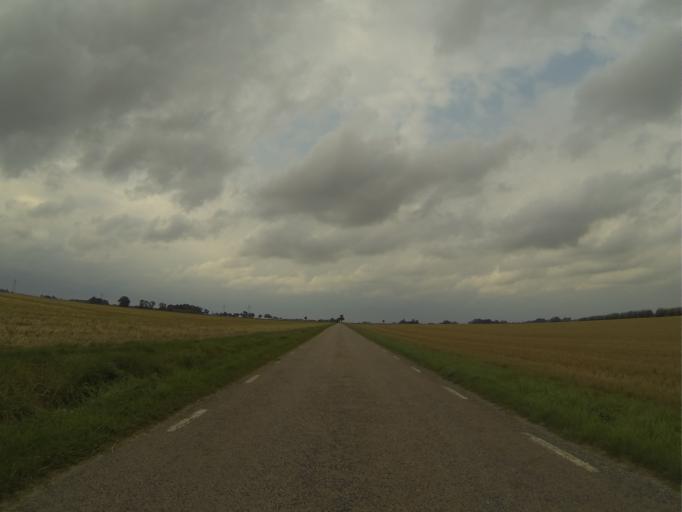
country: SE
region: Skane
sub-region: Kavlinge Kommun
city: Kaevlinge
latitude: 55.7657
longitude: 13.1659
